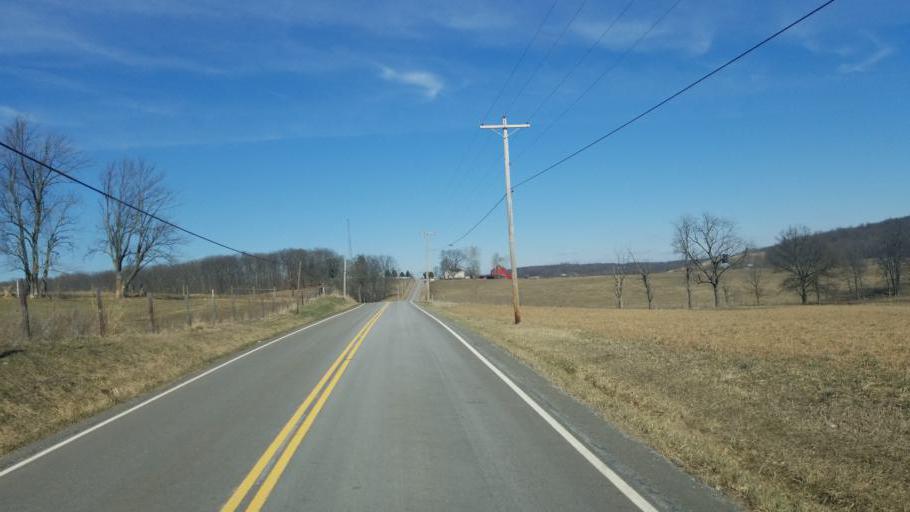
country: US
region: Ohio
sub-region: Knox County
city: Danville
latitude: 40.4719
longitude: -82.2419
